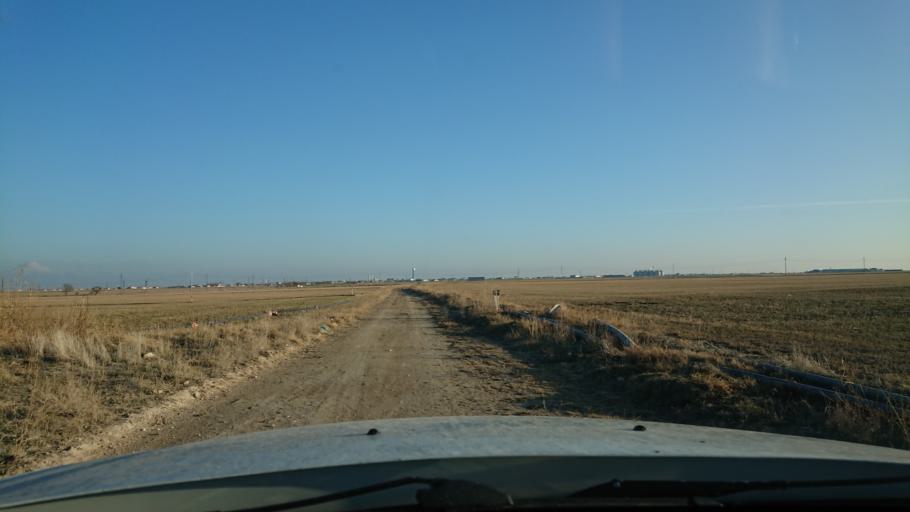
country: TR
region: Aksaray
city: Sultanhani
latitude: 38.2689
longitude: 33.5186
